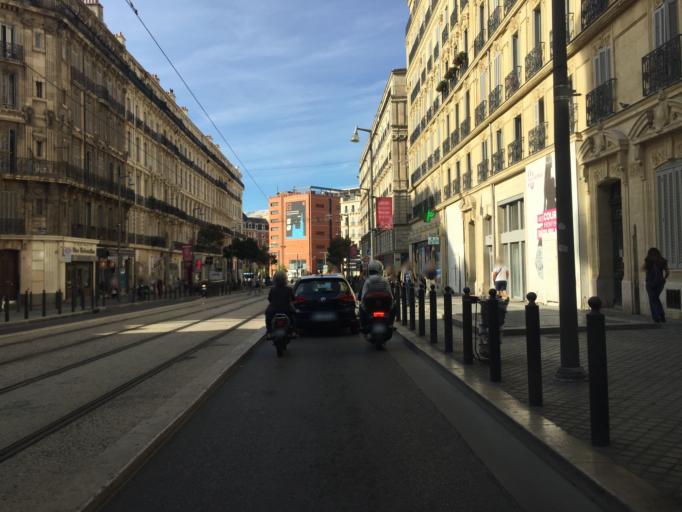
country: FR
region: Provence-Alpes-Cote d'Azur
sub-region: Departement des Bouches-du-Rhone
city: Marseille 02
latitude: 43.3036
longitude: 5.3682
